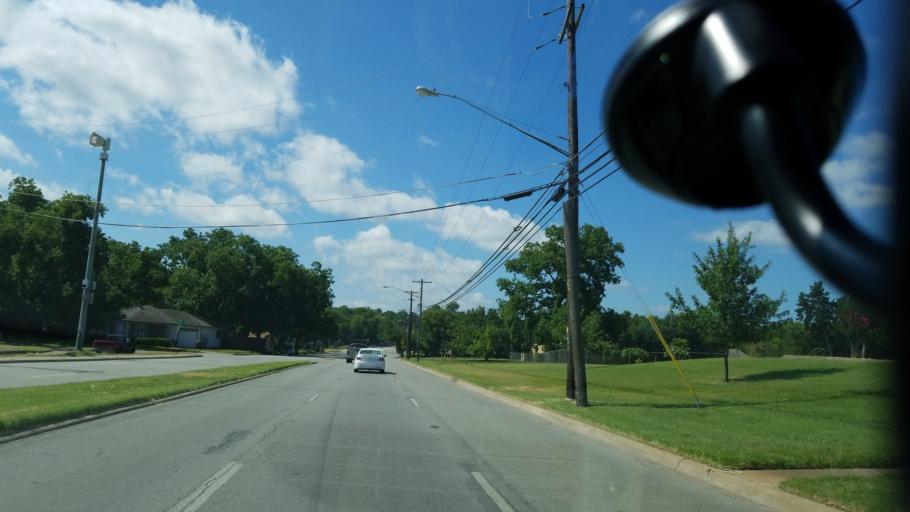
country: US
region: Texas
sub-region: Dallas County
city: Cockrell Hill
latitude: 32.6900
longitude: -96.8147
